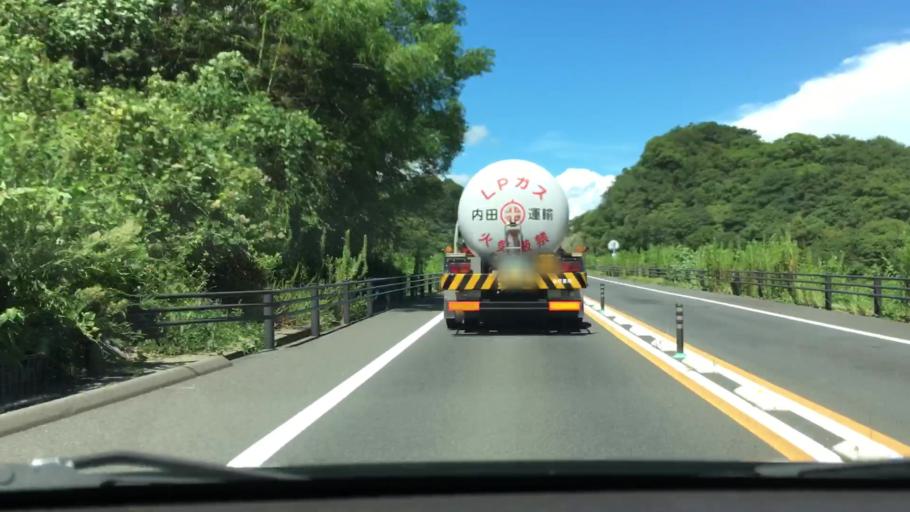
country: JP
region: Nagasaki
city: Sasebo
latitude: 33.0219
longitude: 129.7339
